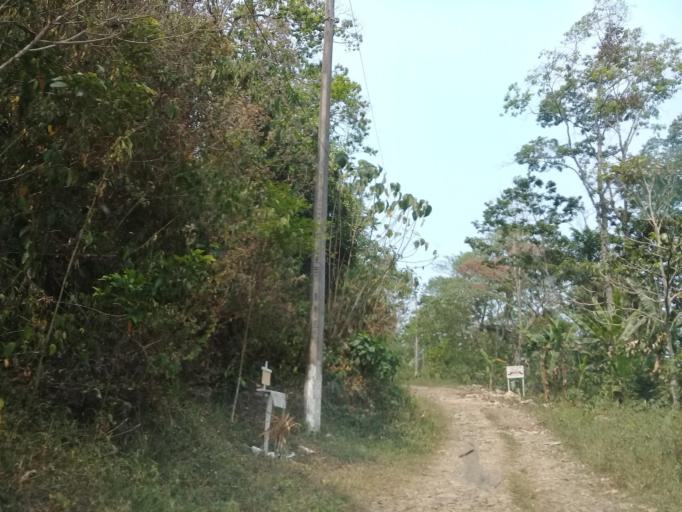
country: MX
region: Veracruz
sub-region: Tezonapa
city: Laguna Chica (Pueblo Nuevo)
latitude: 18.5849
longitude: -96.7480
